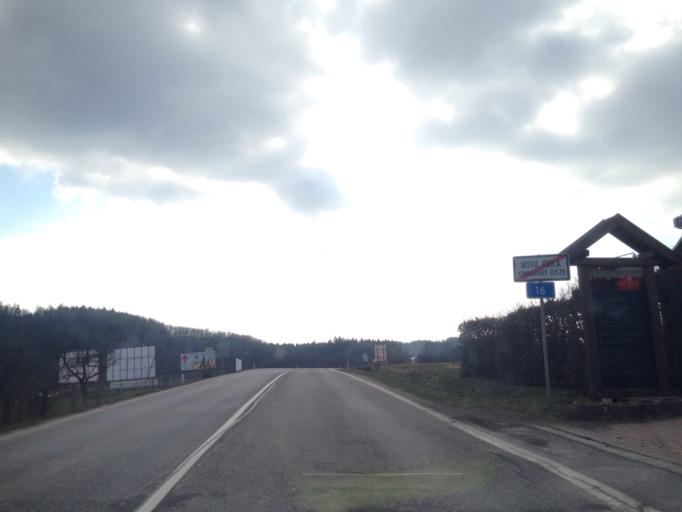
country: CZ
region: Kralovehradecky
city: Nova Paka
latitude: 50.4696
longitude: 15.4986
